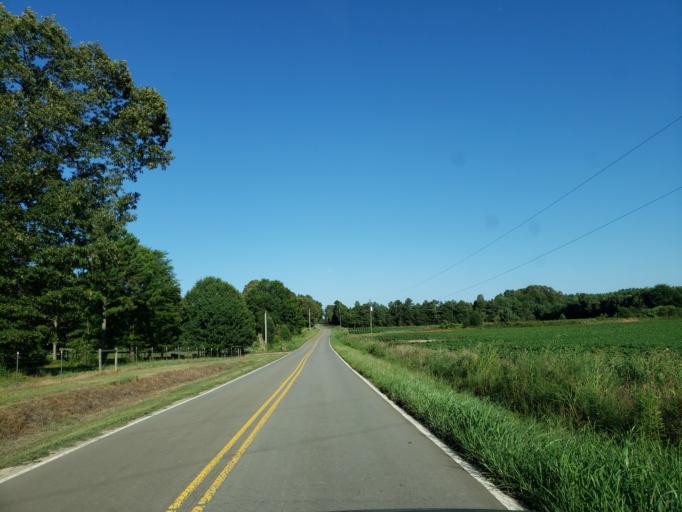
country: US
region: Georgia
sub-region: Polk County
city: Aragon
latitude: 34.1042
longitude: -85.0145
